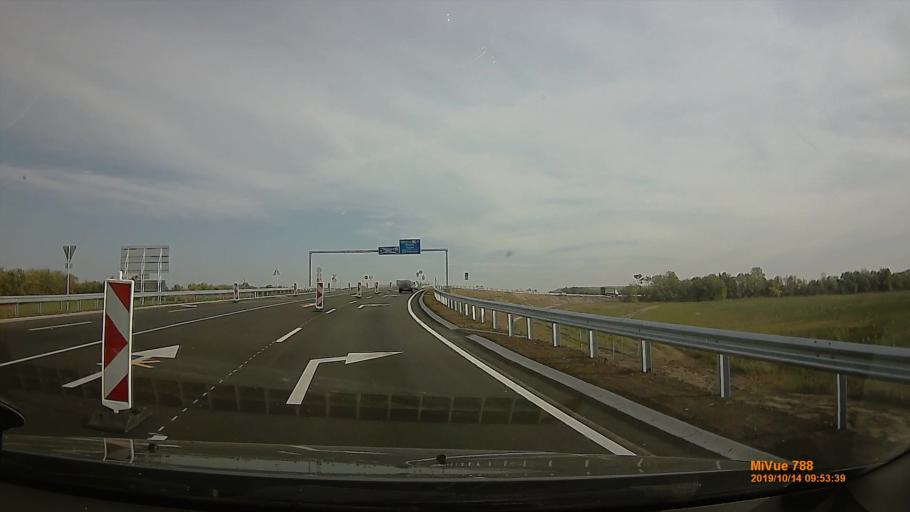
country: HU
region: Pest
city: Albertirsa
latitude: 47.2634
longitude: 19.6149
